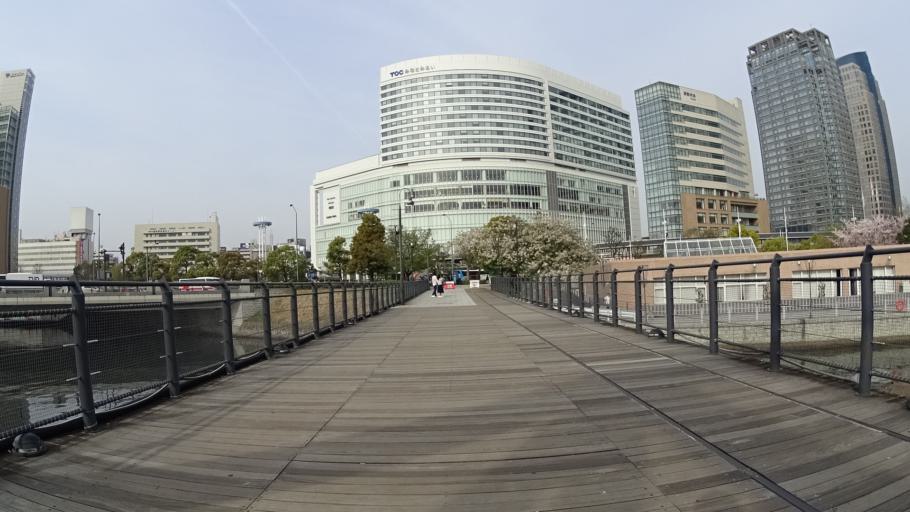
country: JP
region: Kanagawa
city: Yokohama
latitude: 35.4526
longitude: 139.6333
